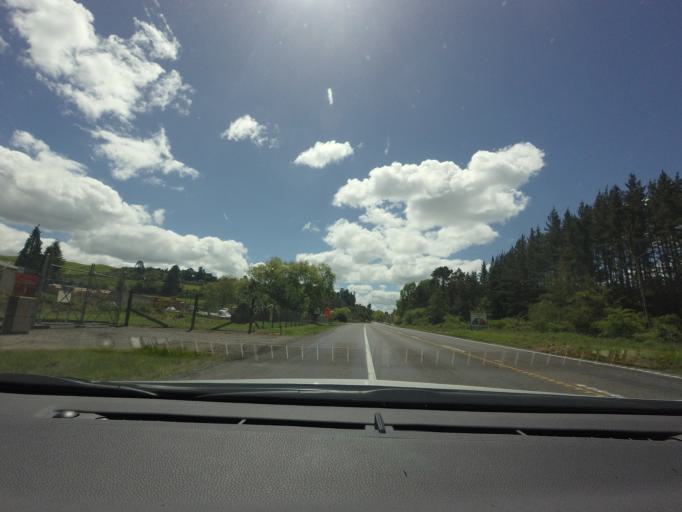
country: NZ
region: Bay of Plenty
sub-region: Rotorua District
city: Rotorua
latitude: -38.1799
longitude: 176.2498
